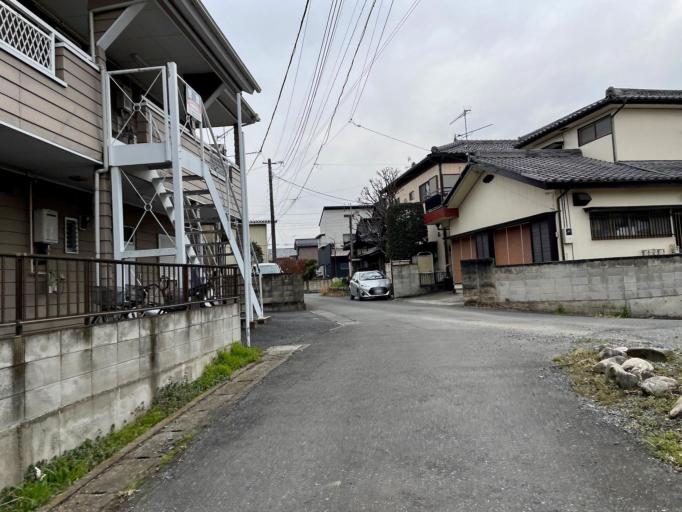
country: JP
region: Saitama
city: Kodamacho-kodamaminami
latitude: 36.1961
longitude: 139.1310
